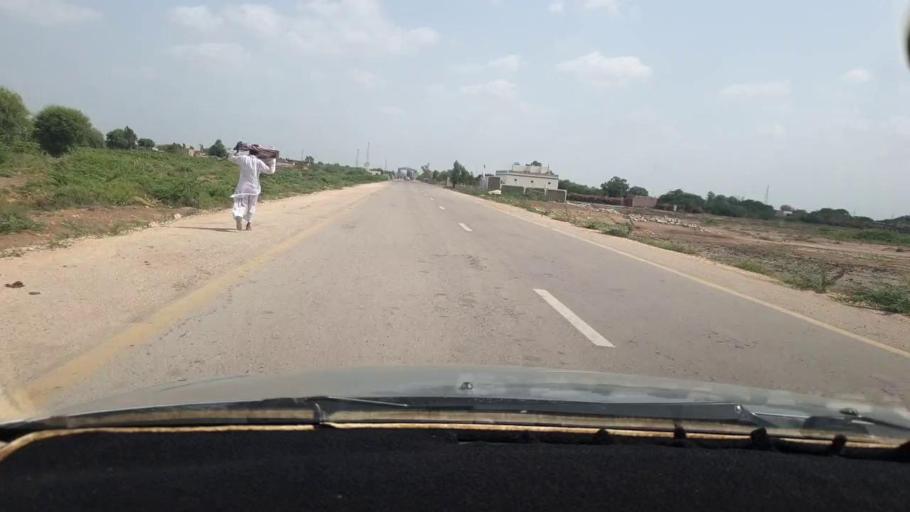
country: PK
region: Sindh
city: Digri
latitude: 25.0862
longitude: 69.1995
